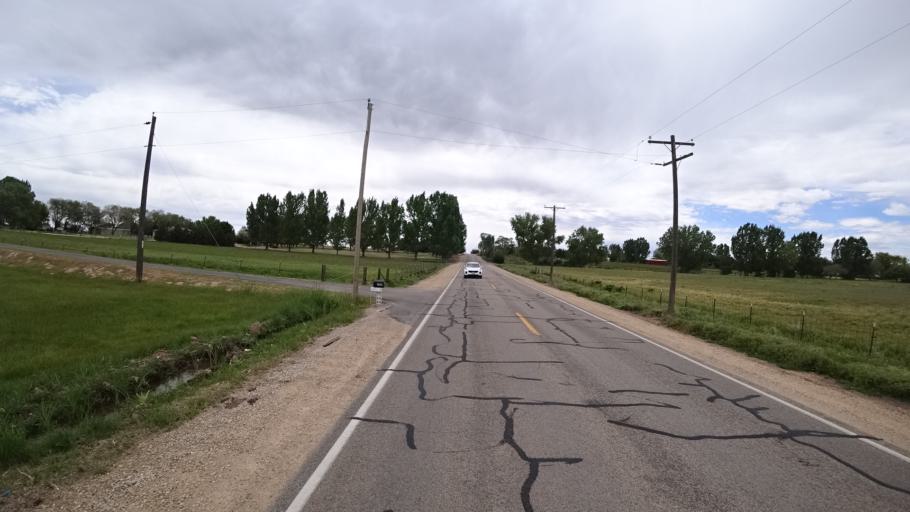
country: US
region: Idaho
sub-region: Ada County
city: Meridian
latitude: 43.5584
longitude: -116.4138
